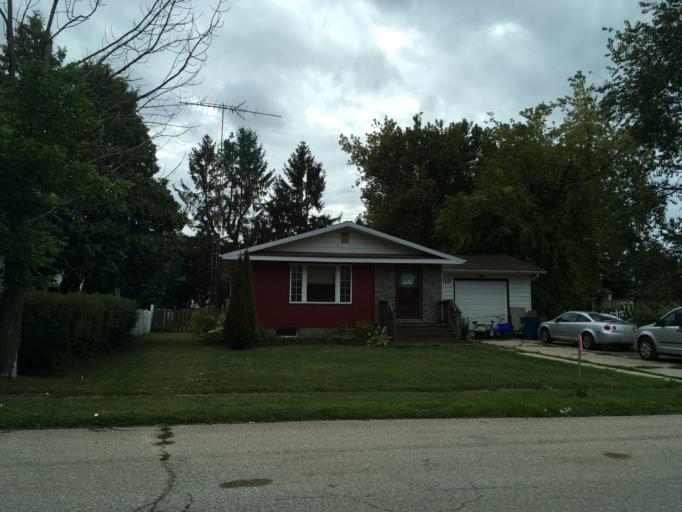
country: US
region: Michigan
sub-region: Tuscola County
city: Caro
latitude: 43.3368
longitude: -83.3555
